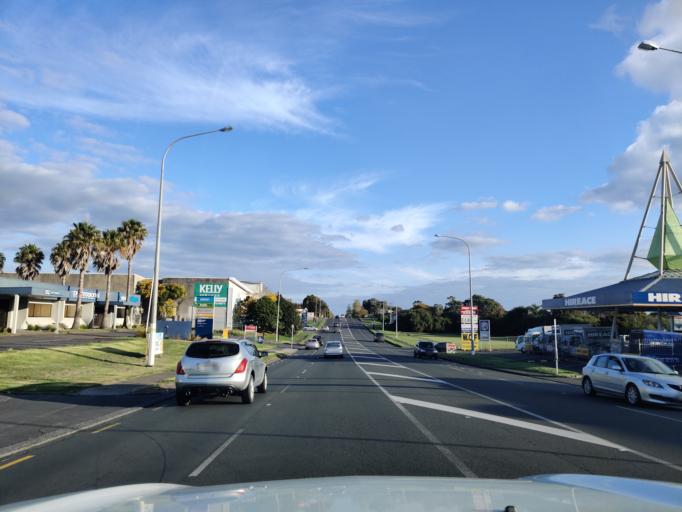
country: NZ
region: Auckland
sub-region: Auckland
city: Manukau City
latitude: -36.9497
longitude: 174.8920
